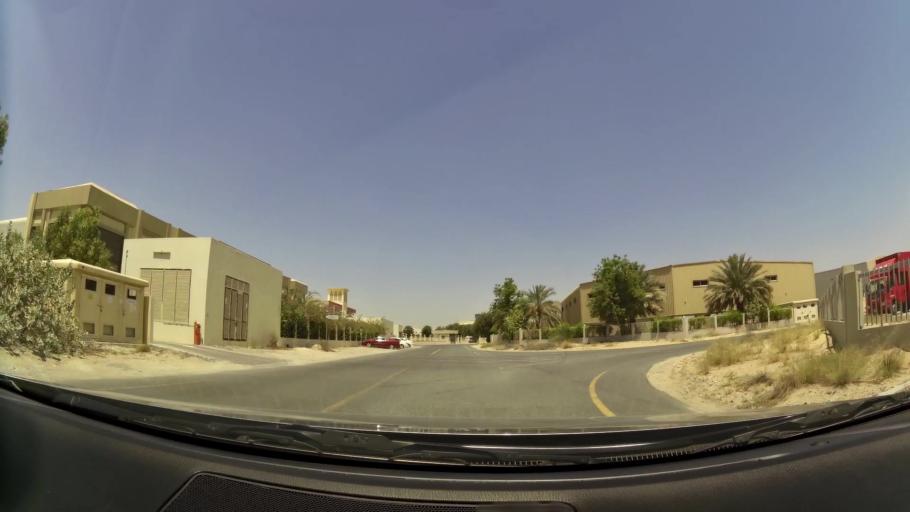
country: AE
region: Dubai
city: Dubai
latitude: 24.9833
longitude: 55.1890
